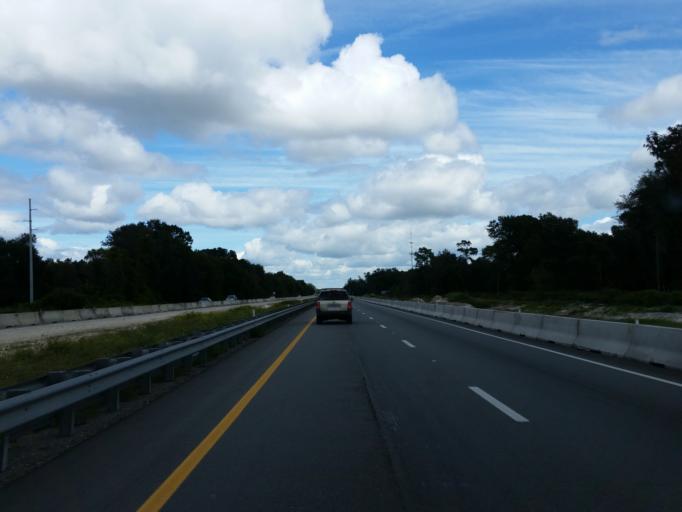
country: US
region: Florida
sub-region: Sumter County
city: Bushnell
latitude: 28.6974
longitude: -82.1271
